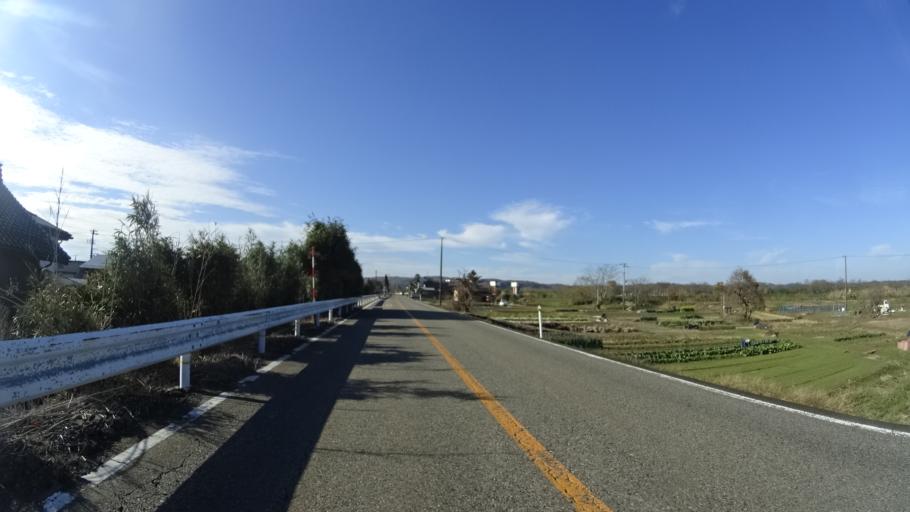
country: JP
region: Niigata
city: Yoshida-kasugacho
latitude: 37.5919
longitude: 138.8401
